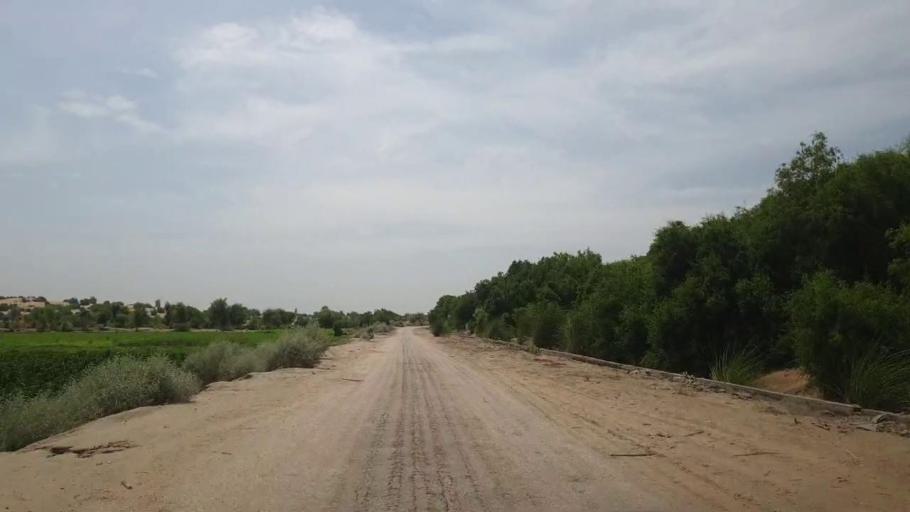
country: PK
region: Sindh
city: Kot Diji
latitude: 27.1038
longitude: 69.0789
